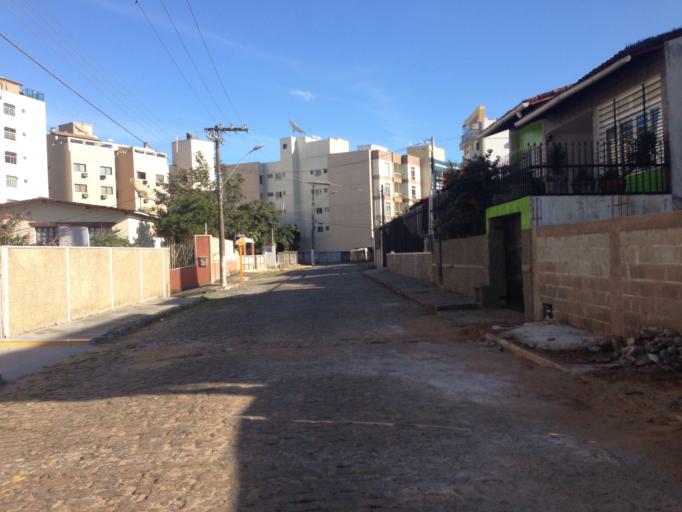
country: BR
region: Espirito Santo
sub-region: Guarapari
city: Guarapari
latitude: -20.6694
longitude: -40.4947
